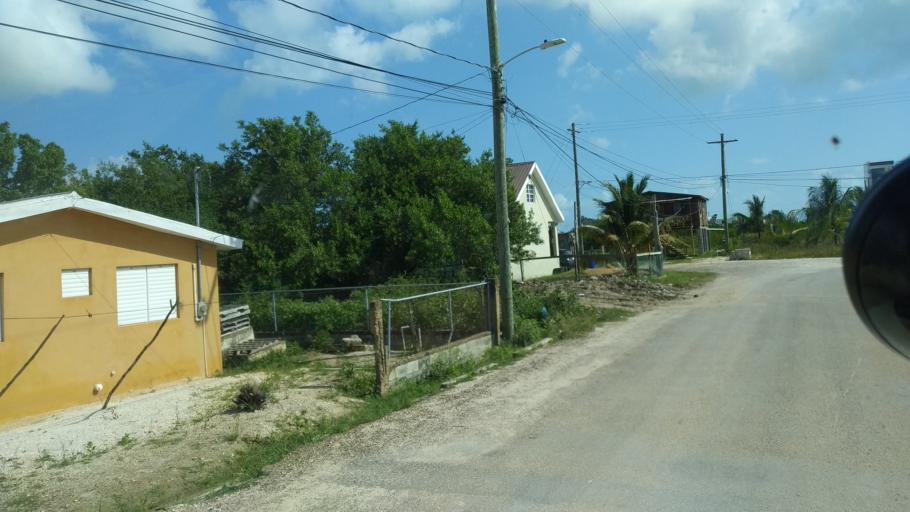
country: BZ
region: Belize
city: Belize City
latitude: 17.5172
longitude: -88.2338
